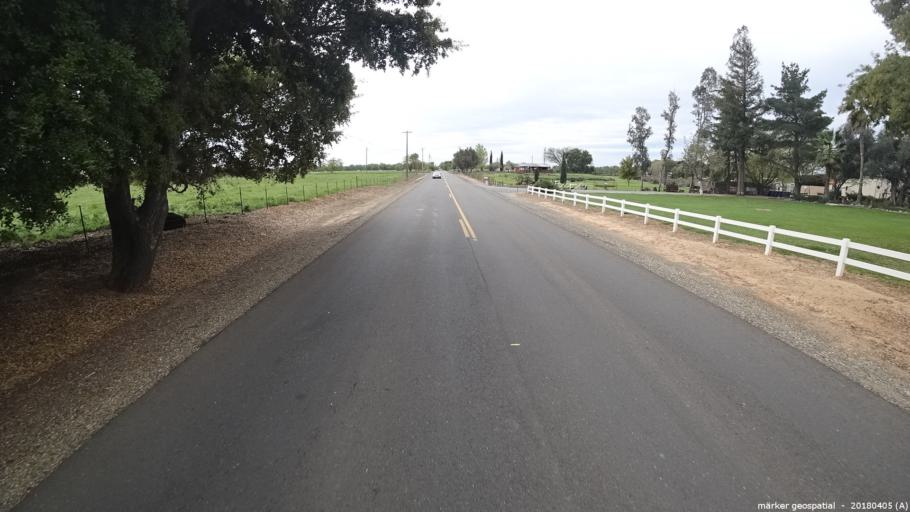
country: US
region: California
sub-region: Sacramento County
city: Galt
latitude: 38.2851
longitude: -121.3374
